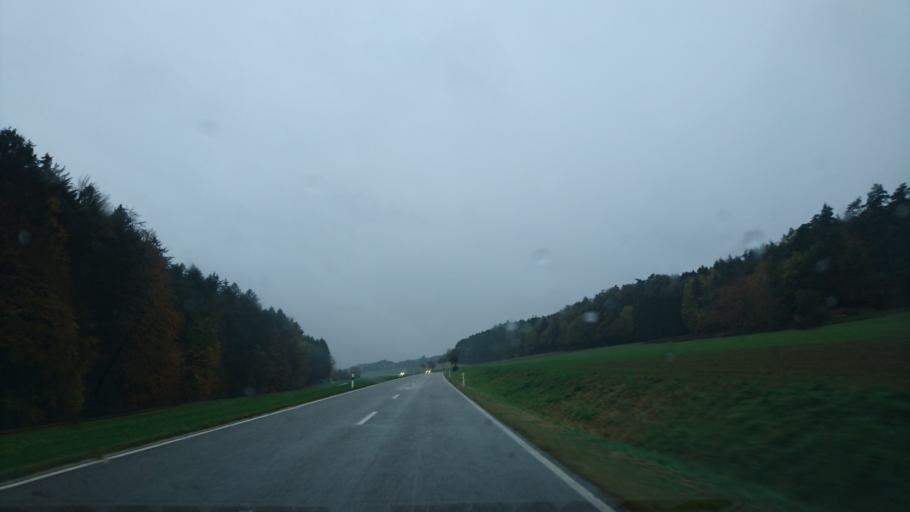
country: DE
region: Bavaria
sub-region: Swabia
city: Schiltberg
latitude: 48.4535
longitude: 11.2362
